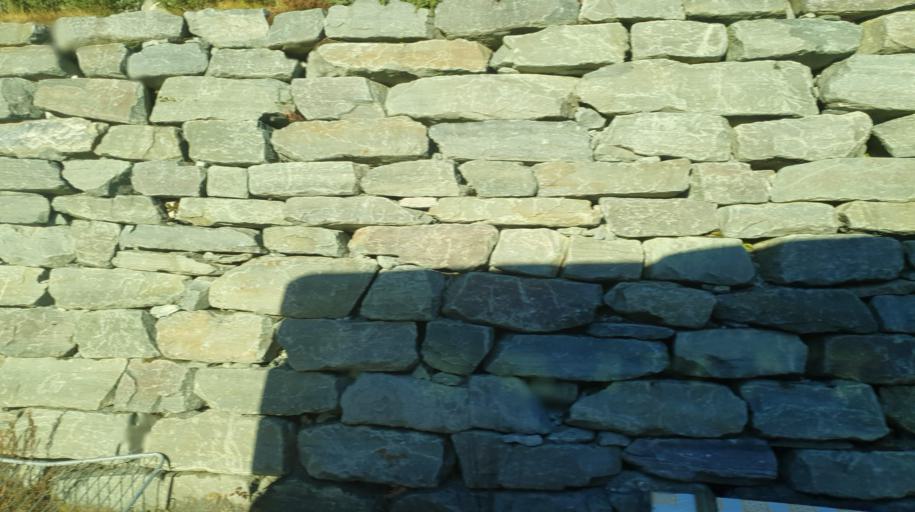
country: NO
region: Buskerud
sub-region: Krodsherad
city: Noresund
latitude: 60.2271
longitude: 9.5205
